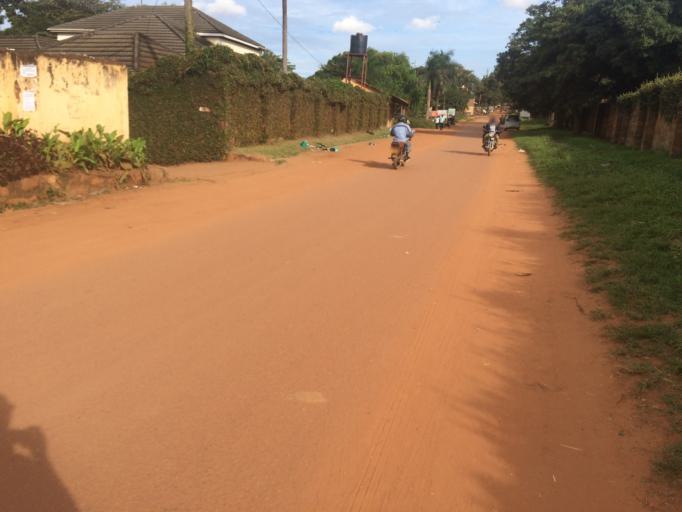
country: UG
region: Central Region
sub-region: Kampala District
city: Kampala
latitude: 0.2961
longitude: 32.5945
